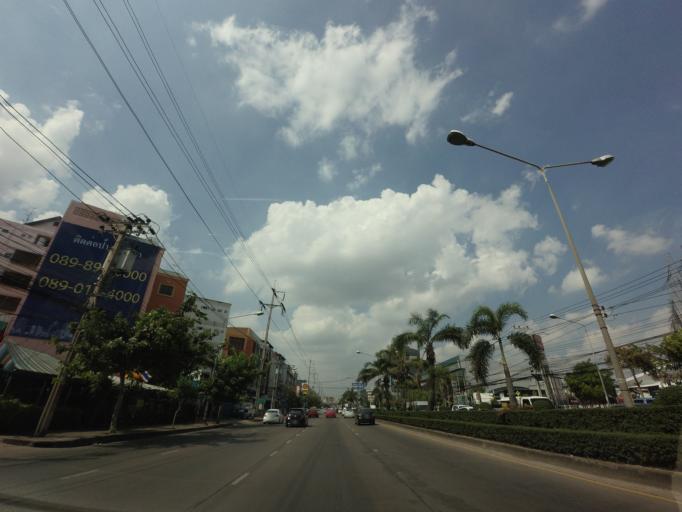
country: TH
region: Bangkok
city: Chatuchak
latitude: 13.8532
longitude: 100.5512
